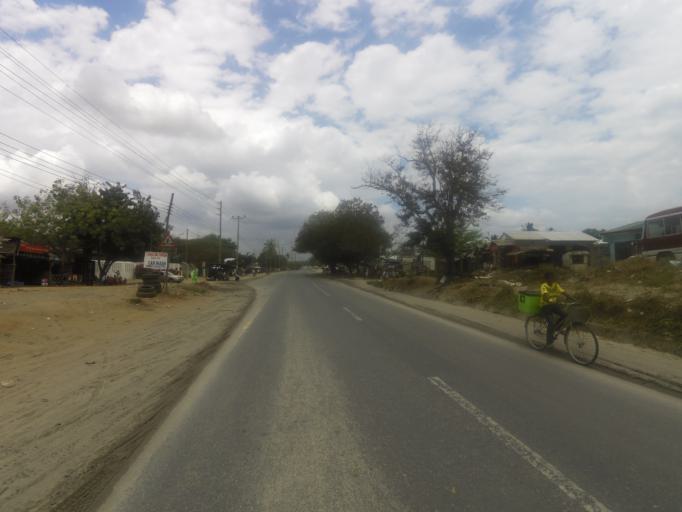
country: TZ
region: Pwani
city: Vikindu
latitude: -6.9457
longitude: 39.2800
